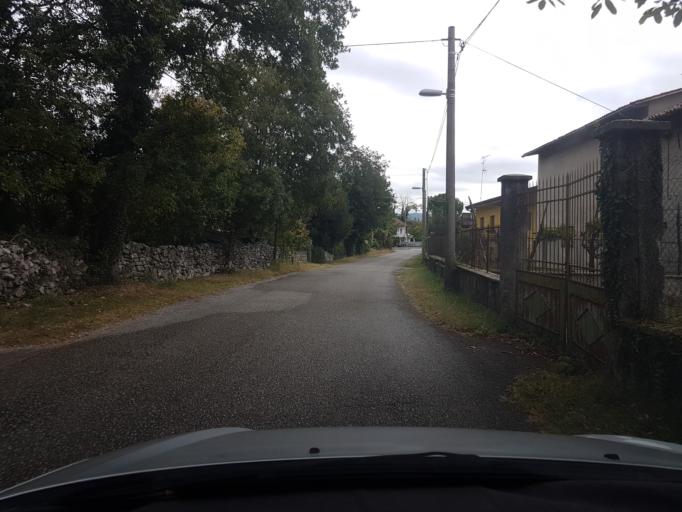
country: IT
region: Friuli Venezia Giulia
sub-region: Provincia di Gorizia
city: Doberdo del Lago
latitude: 45.8235
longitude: 13.5778
